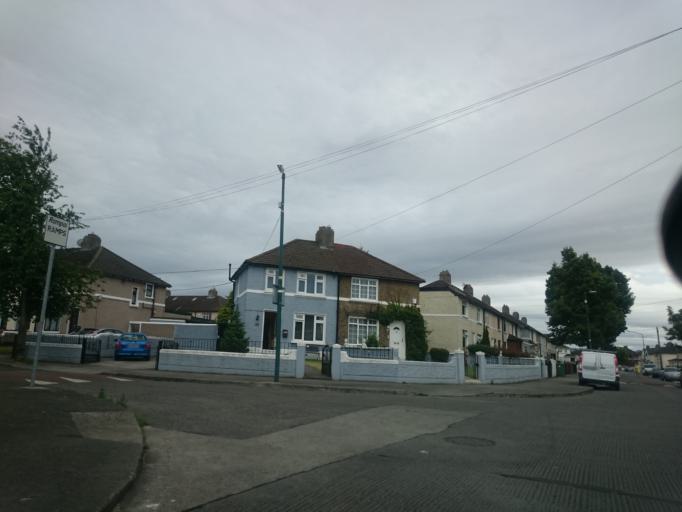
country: IE
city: Greenhills
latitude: 53.3263
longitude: -6.3060
